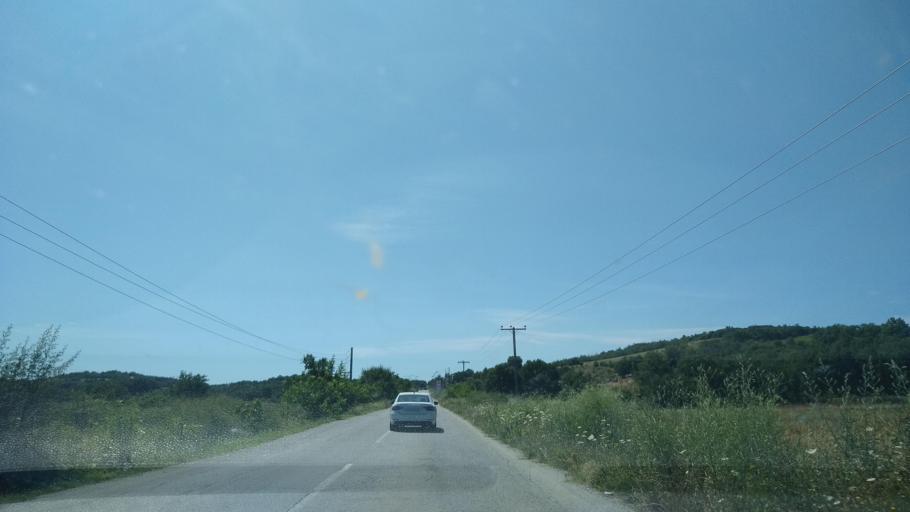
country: GR
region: Central Macedonia
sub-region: Nomos Chalkidikis
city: Megali Panagia
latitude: 40.4211
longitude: 23.6880
